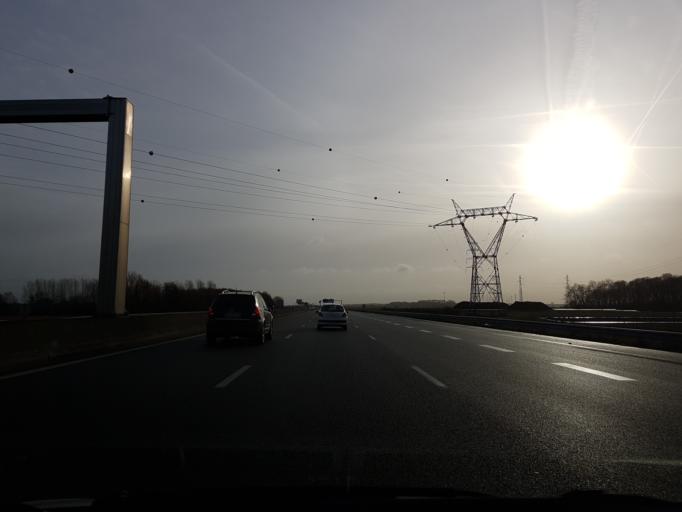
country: FR
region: Ile-de-France
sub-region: Departement de Seine-et-Marne
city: Moissy-Cramayel
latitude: 48.5988
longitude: 2.6060
